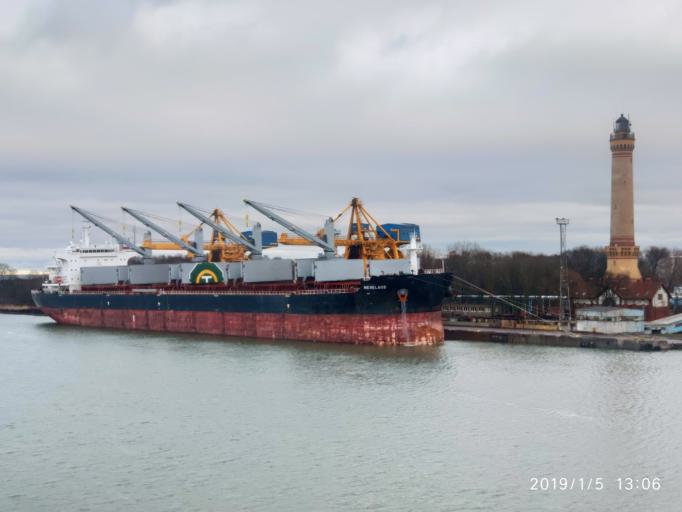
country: PL
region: West Pomeranian Voivodeship
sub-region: Swinoujscie
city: Swinoujscie
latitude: 53.9150
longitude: 14.2797
